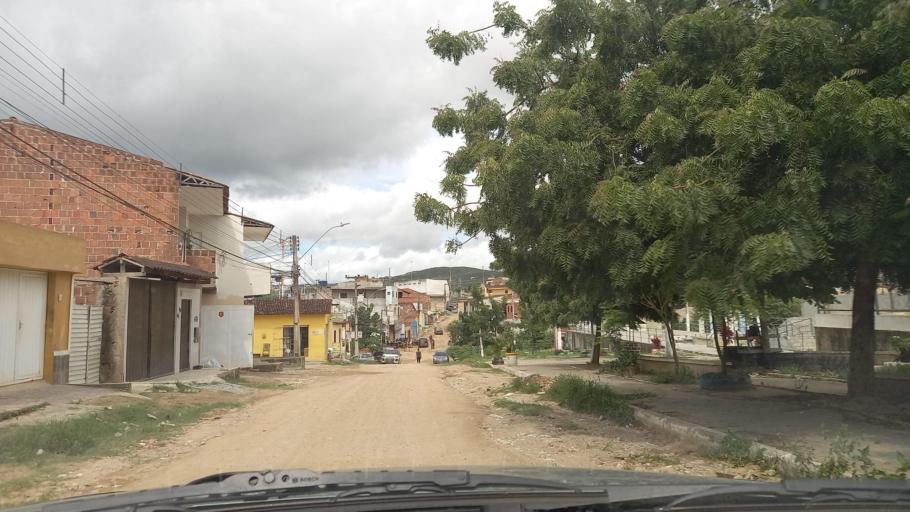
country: BR
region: Pernambuco
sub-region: Gravata
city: Gravata
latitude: -8.1948
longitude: -35.5778
